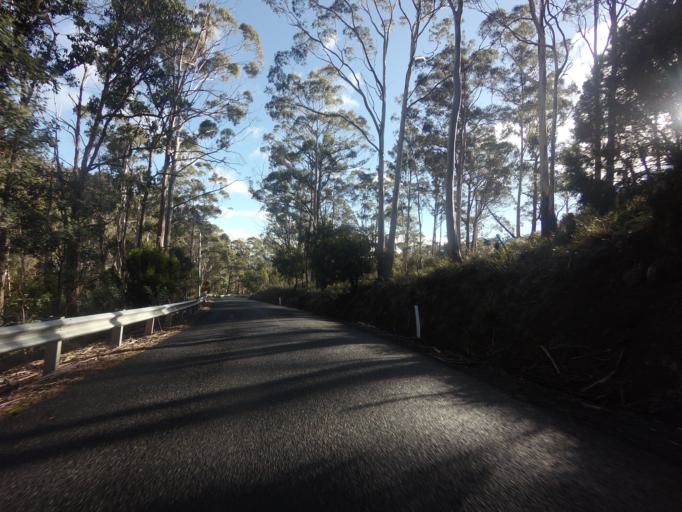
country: AU
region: Tasmania
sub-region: Glenorchy
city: Berriedale
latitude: -42.8141
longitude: 147.1752
